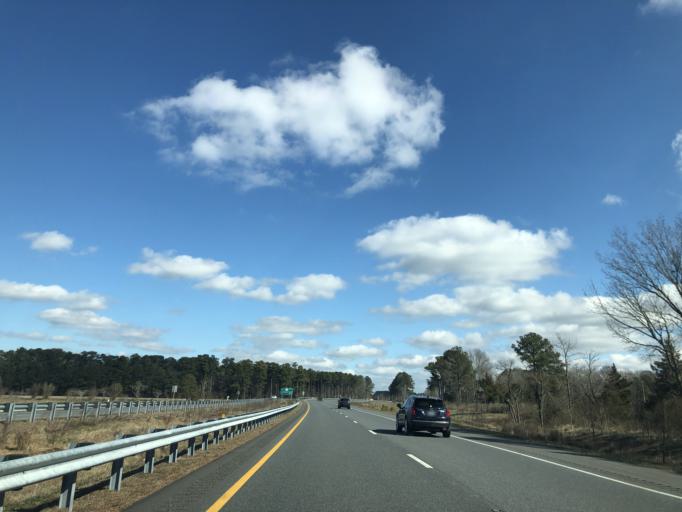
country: US
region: Maryland
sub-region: Worcester County
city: Snow Hill
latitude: 38.2409
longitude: -75.3057
